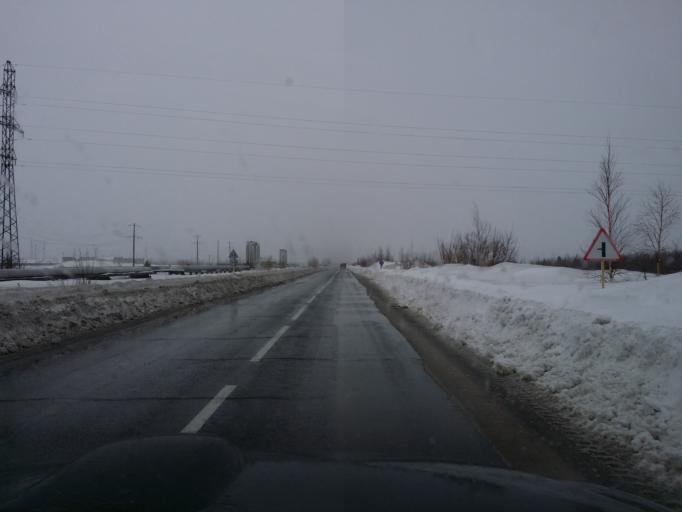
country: RU
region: Khanty-Mansiyskiy Avtonomnyy Okrug
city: Izluchinsk
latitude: 60.9790
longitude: 76.9014
